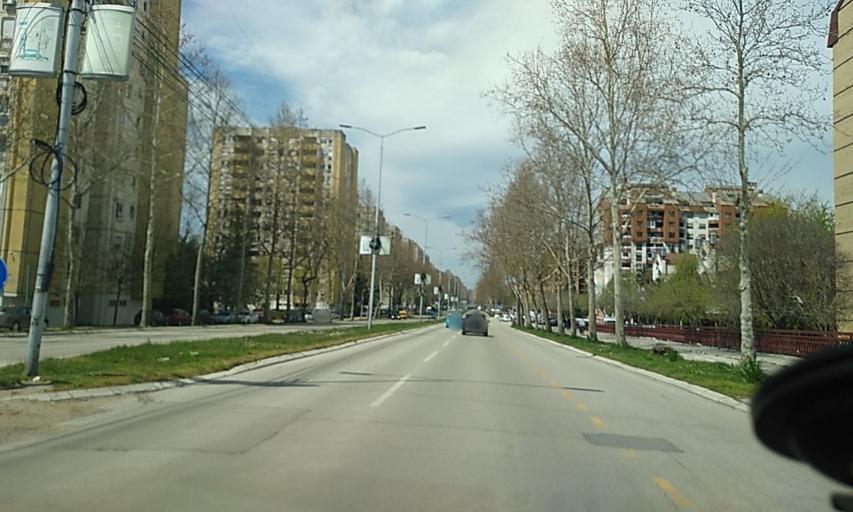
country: RS
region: Central Serbia
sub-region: Nisavski Okrug
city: Nis
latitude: 43.3167
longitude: 21.9251
